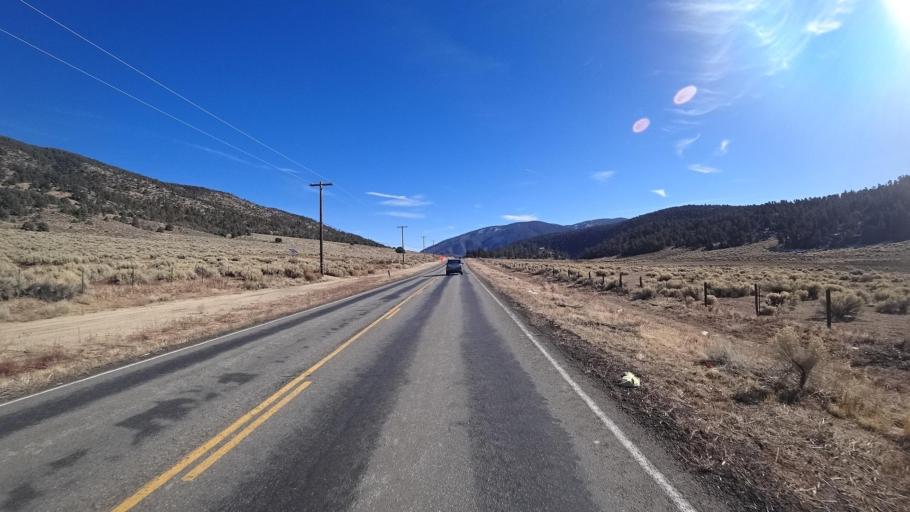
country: US
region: California
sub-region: Kern County
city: Frazier Park
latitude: 34.8332
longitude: -119.0339
